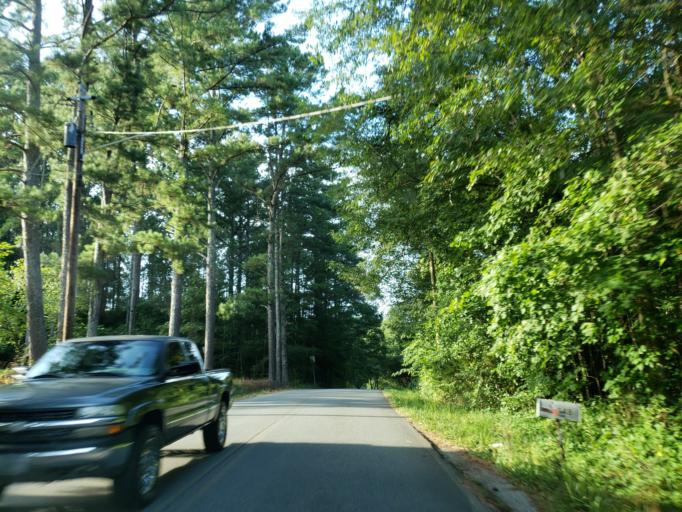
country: US
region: Georgia
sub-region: Bartow County
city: Euharlee
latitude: 34.2372
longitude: -84.9546
